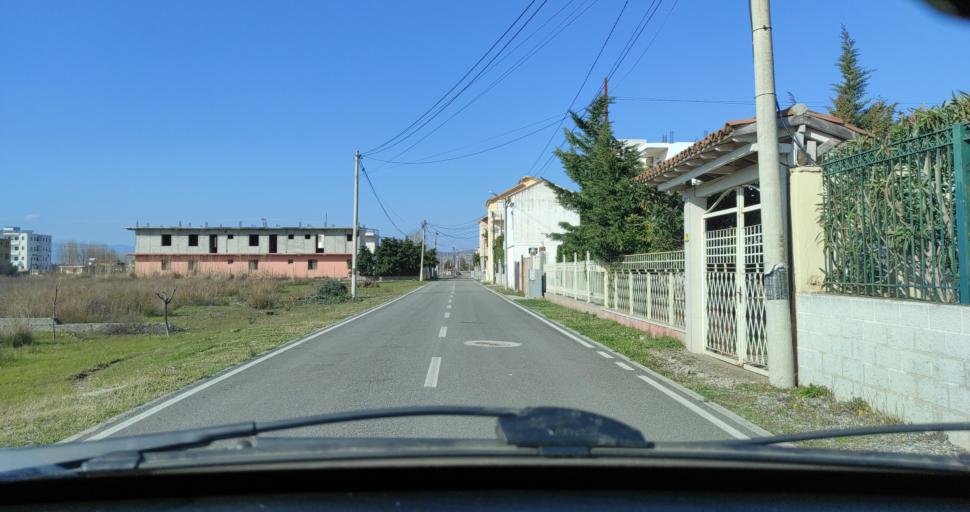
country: AL
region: Shkoder
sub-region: Rrethi i Shkodres
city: Velipoje
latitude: 41.8636
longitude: 19.4353
